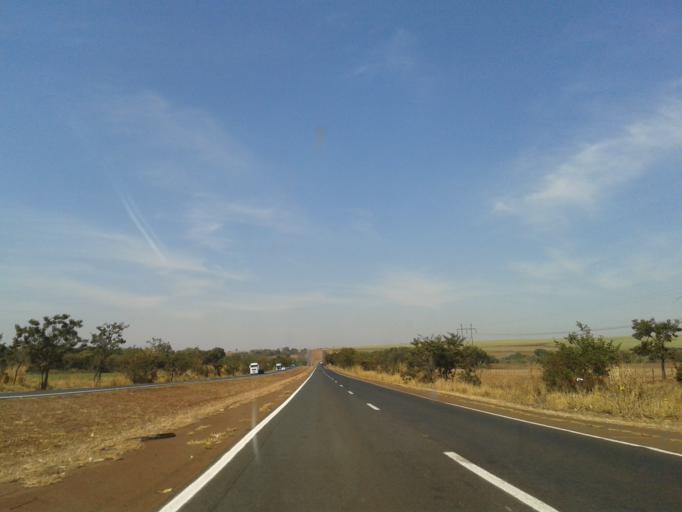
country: BR
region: Goias
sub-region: Itumbiara
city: Itumbiara
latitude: -18.2210
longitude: -49.2682
